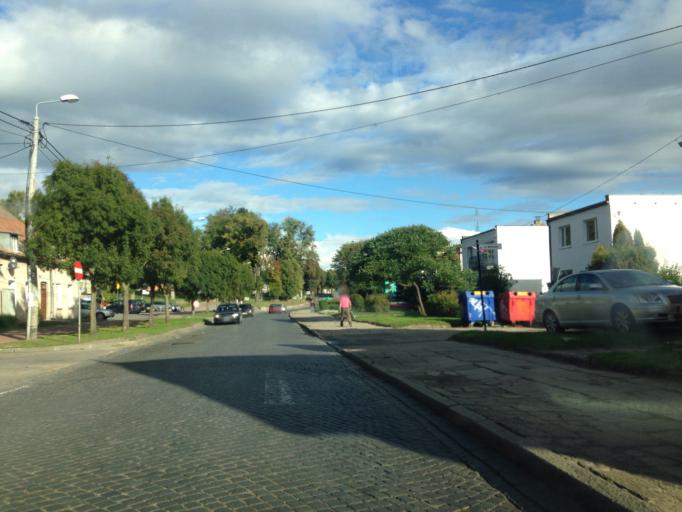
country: PL
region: Warmian-Masurian Voivodeship
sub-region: Powiat ilawski
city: Susz
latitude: 53.7194
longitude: 19.3441
